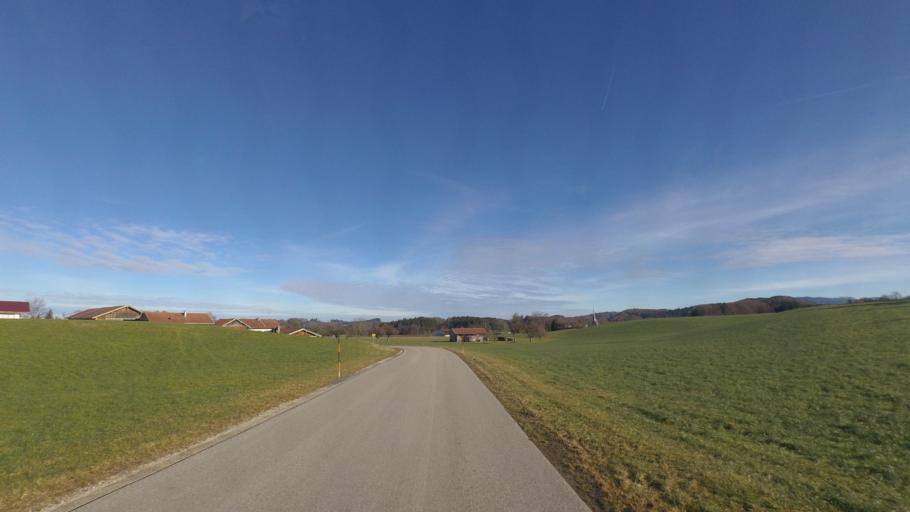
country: DE
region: Bavaria
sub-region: Upper Bavaria
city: Bergen
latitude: 47.8355
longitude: 12.5785
